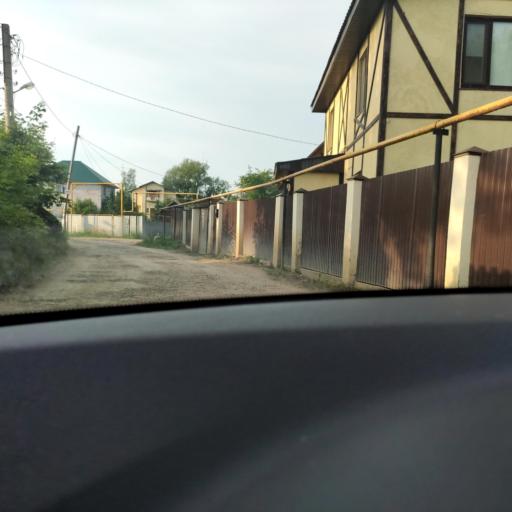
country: RU
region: Samara
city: Rozhdestveno
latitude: 53.1503
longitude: 50.0246
